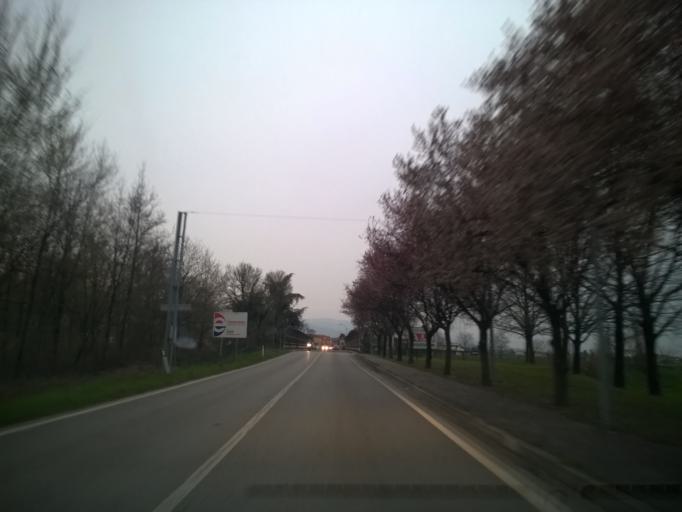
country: IT
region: Veneto
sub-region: Provincia di Vicenza
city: Villaverla
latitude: 45.6737
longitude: 11.4678
